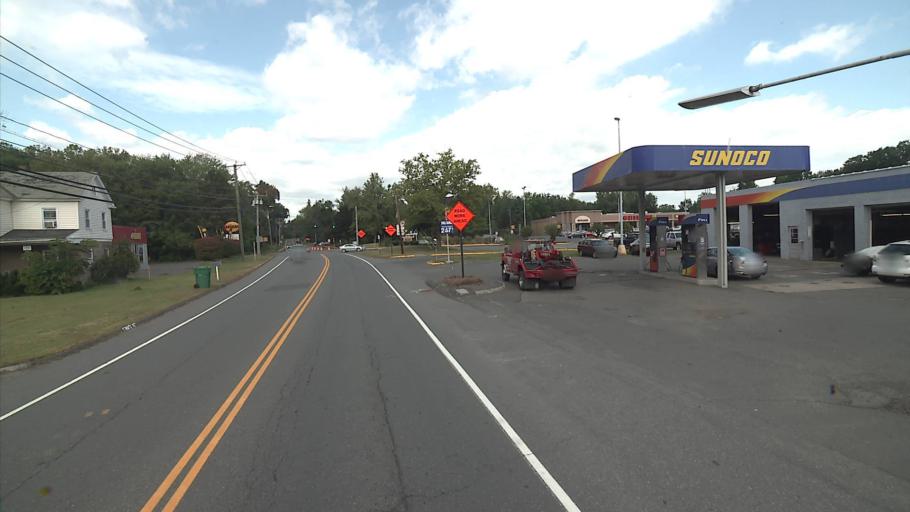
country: US
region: Connecticut
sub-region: Hartford County
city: Blue Hills
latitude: 41.8353
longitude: -72.7377
